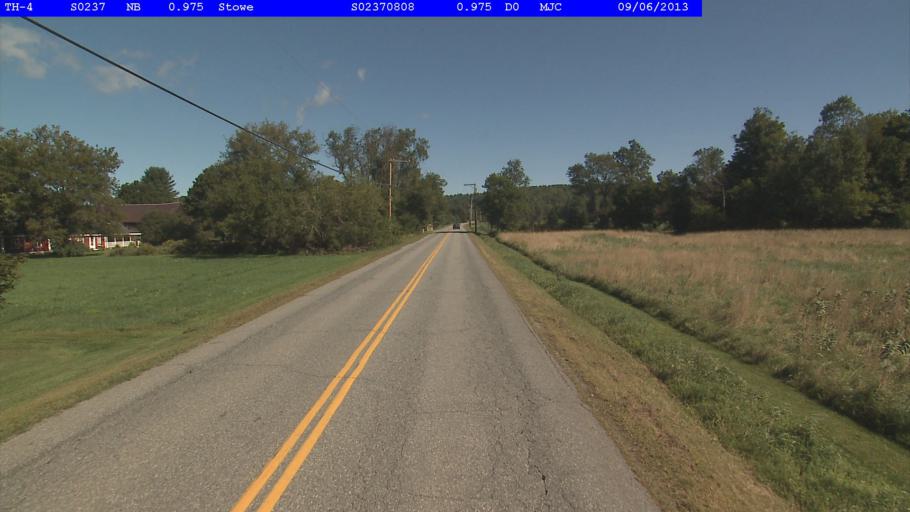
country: US
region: Vermont
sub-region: Lamoille County
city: Morristown
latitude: 44.4948
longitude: -72.6585
